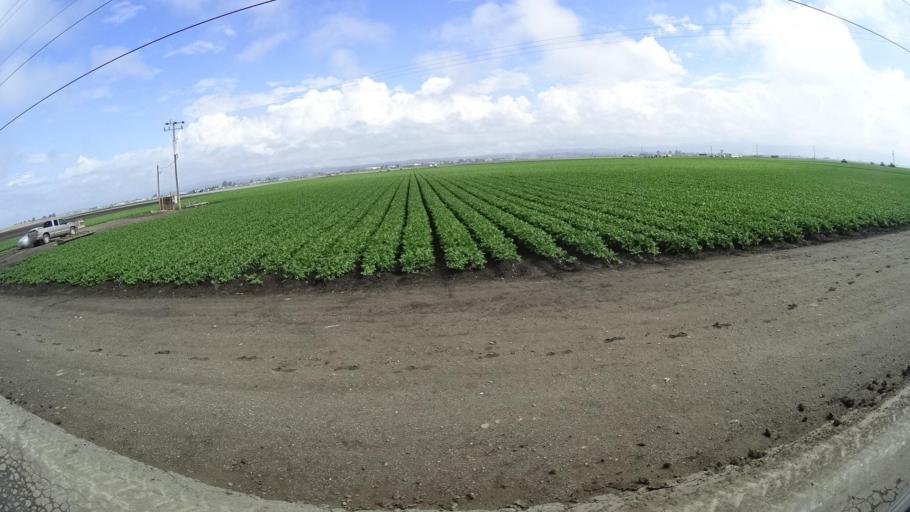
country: US
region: California
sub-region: Monterey County
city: Castroville
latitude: 36.7380
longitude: -121.7627
